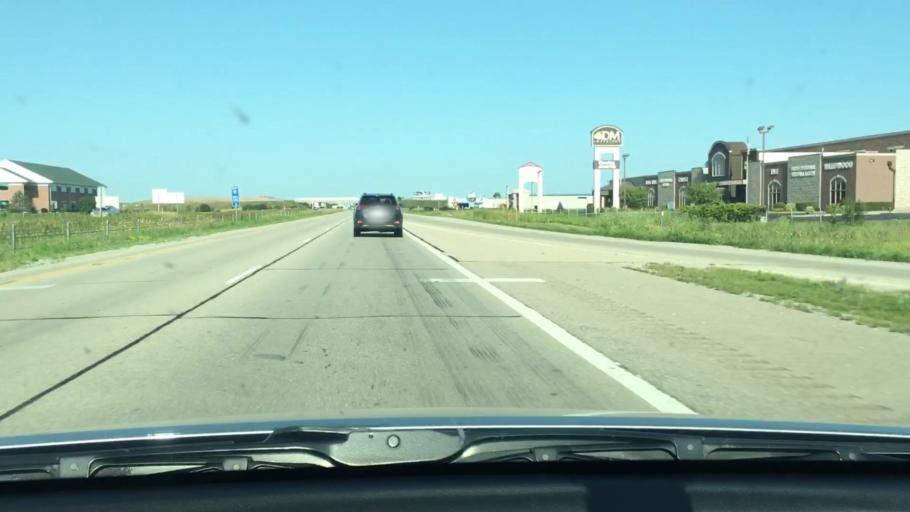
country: US
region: Wisconsin
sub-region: Outagamie County
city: Little Chute
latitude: 44.2981
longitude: -88.3158
